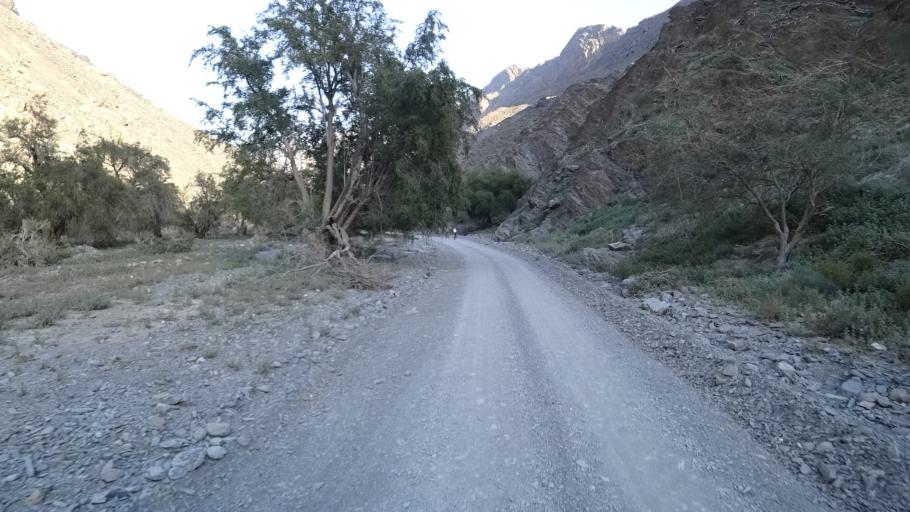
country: OM
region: Al Batinah
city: Bayt al `Awabi
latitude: 23.2546
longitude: 57.4029
